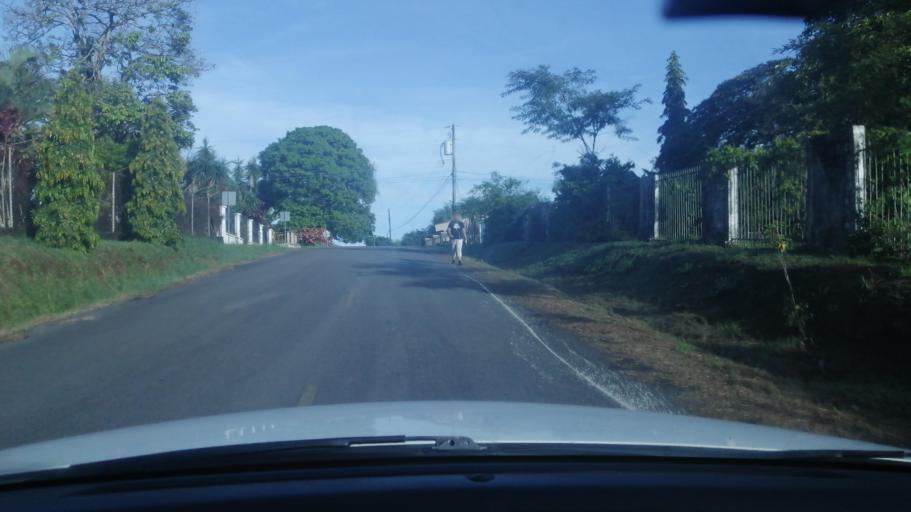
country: PA
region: Chiriqui
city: Mata del Nance
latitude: 8.4472
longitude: -82.4181
